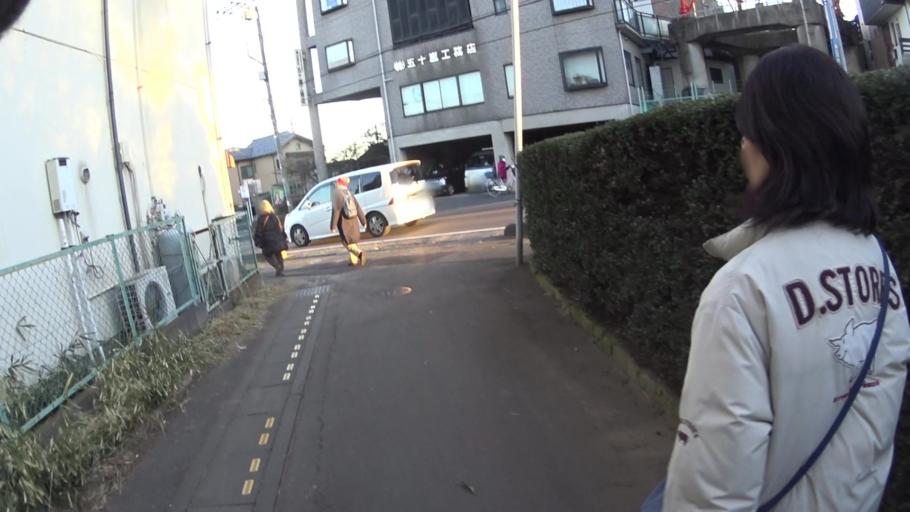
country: JP
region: Saitama
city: Koshigaya
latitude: 35.8839
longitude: 139.7353
